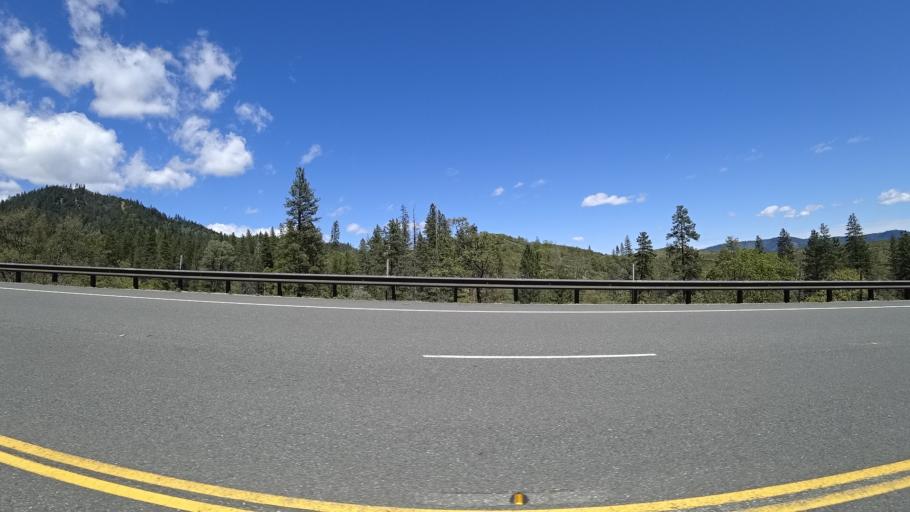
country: US
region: California
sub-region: Trinity County
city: Weaverville
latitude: 40.7460
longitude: -122.9713
